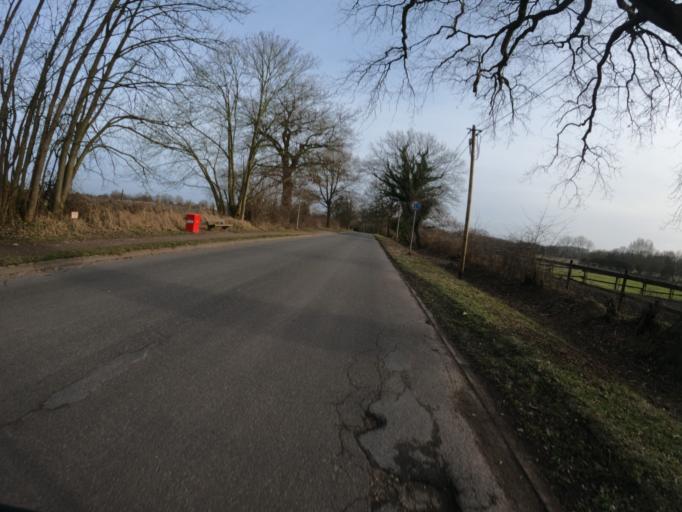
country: DE
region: Schleswig-Holstein
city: Halstenbek
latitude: 53.5793
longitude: 9.8386
